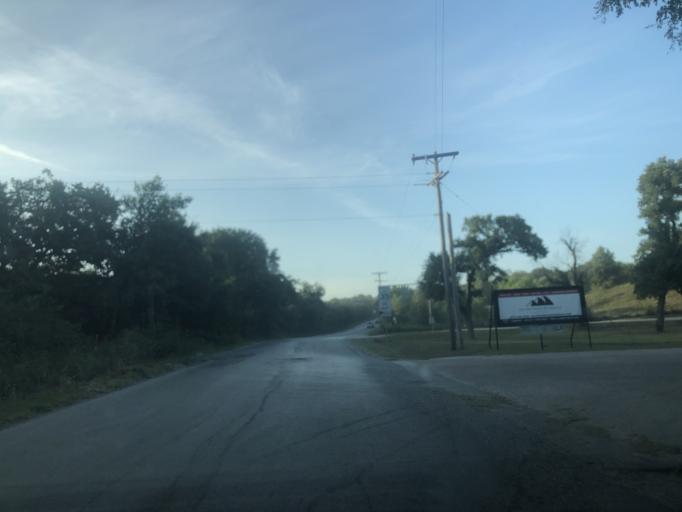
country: US
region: Texas
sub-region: Tarrant County
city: Lakeside
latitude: 32.7922
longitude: -97.4924
